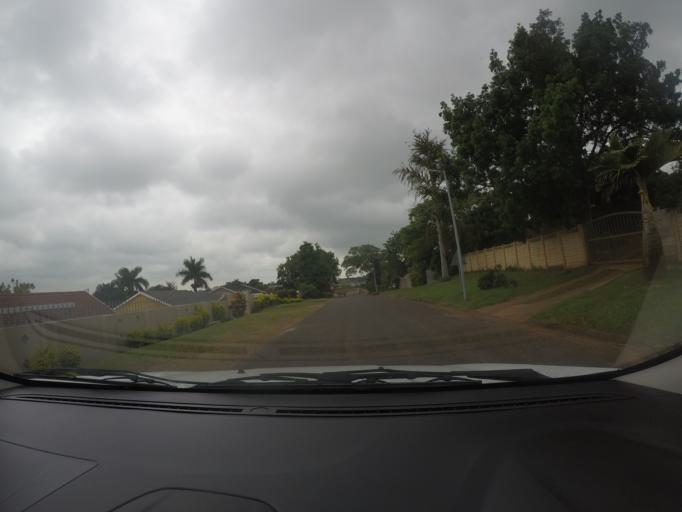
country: ZA
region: KwaZulu-Natal
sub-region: uThungulu District Municipality
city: Empangeni
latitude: -28.7646
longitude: 31.9008
